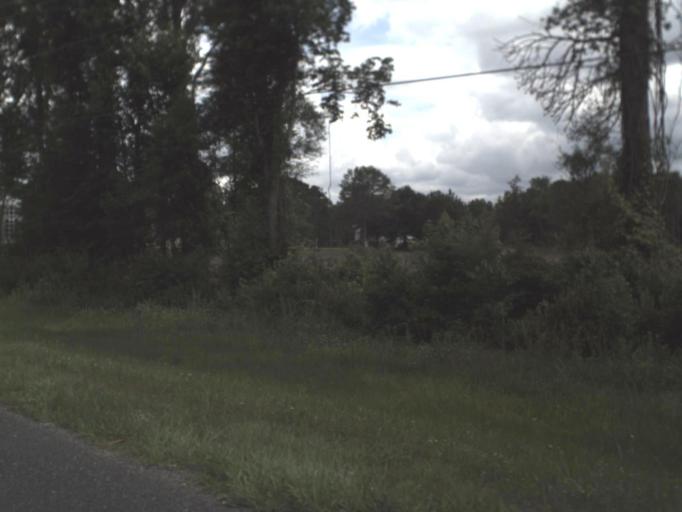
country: US
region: Florida
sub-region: Nassau County
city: Callahan
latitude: 30.5459
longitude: -81.8169
